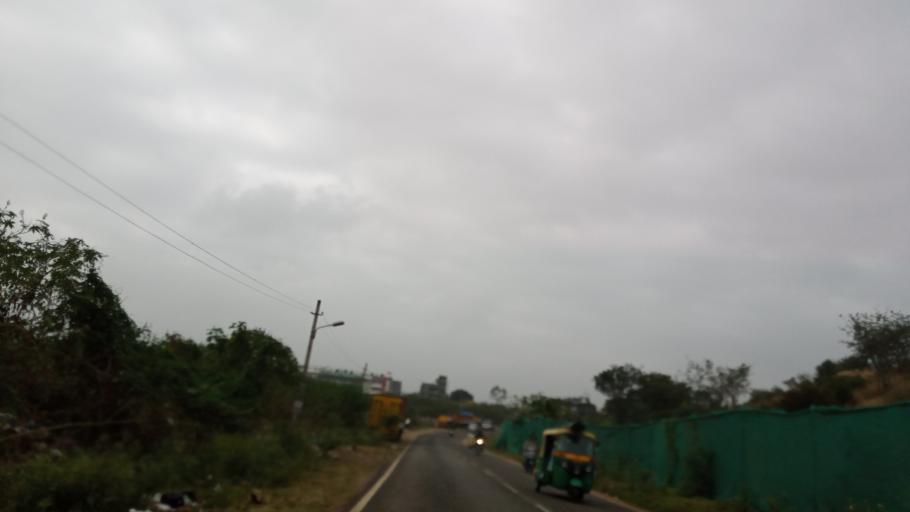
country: IN
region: Karnataka
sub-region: Bangalore Urban
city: Bangalore
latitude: 12.9065
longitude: 77.5331
